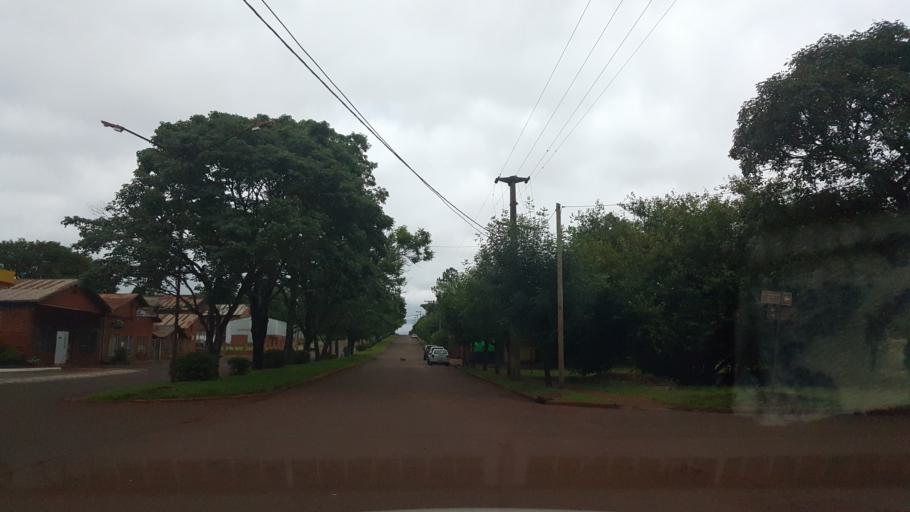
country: AR
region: Misiones
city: Ruiz de Montoya
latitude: -26.9686
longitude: -55.0573
